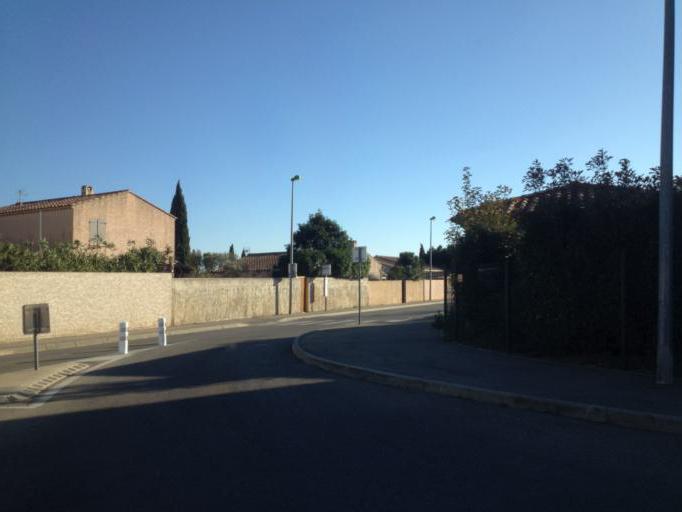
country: FR
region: Provence-Alpes-Cote d'Azur
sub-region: Departement des Bouches-du-Rhone
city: Istres
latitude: 43.5114
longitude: 4.9674
